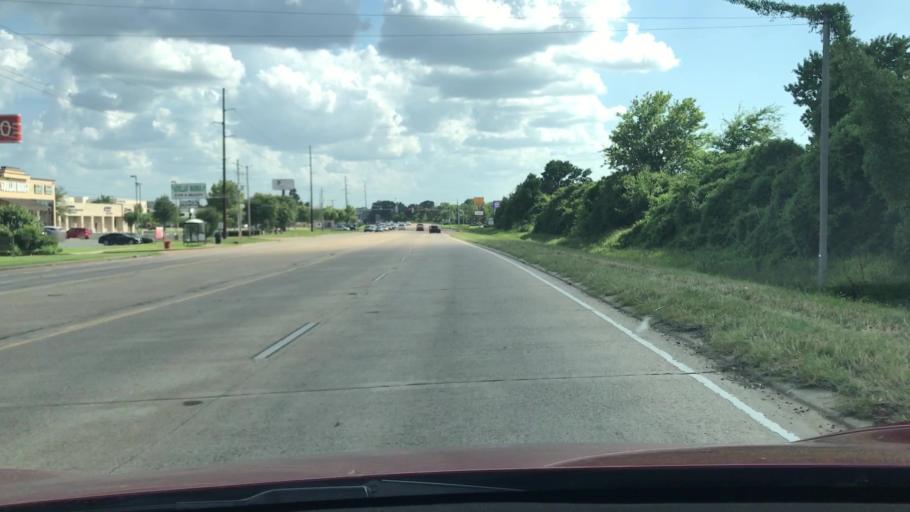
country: US
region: Louisiana
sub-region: Bossier Parish
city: Bossier City
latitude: 32.4295
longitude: -93.7162
